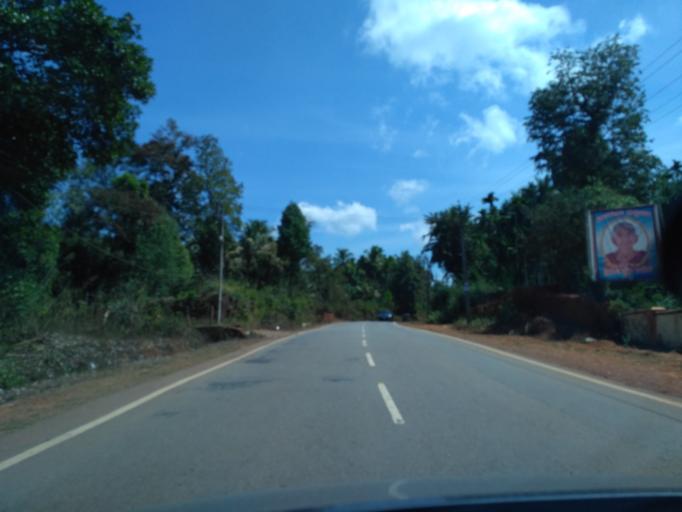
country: IN
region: Karnataka
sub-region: Dakshina Kannada
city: Sulya
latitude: 12.5198
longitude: 75.4468
